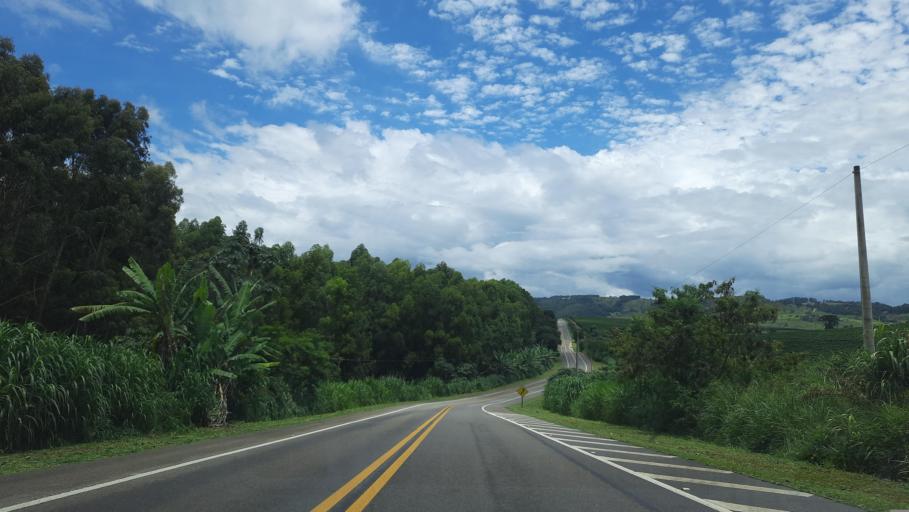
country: BR
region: Sao Paulo
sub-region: Vargem Grande Do Sul
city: Vargem Grande do Sul
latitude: -21.8035
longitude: -46.7956
